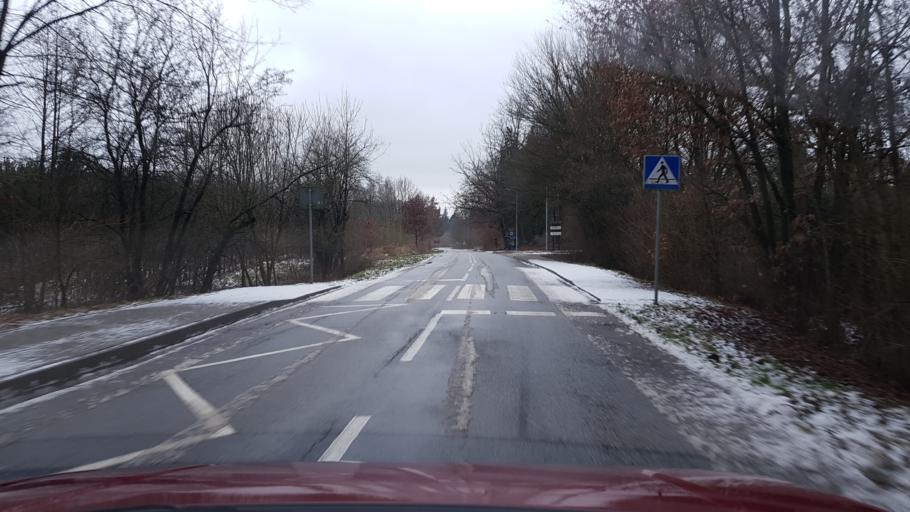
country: PL
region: West Pomeranian Voivodeship
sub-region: Powiat gryficki
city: Ploty
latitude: 53.7202
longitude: 15.3060
